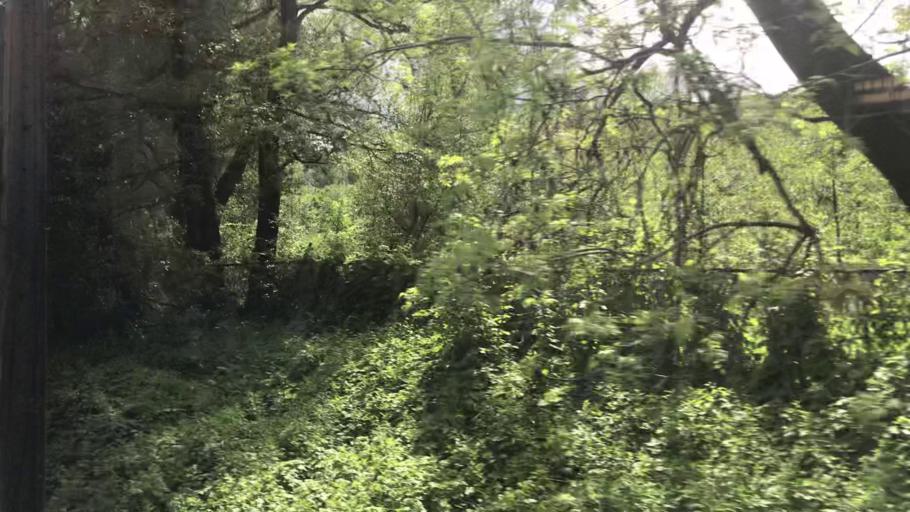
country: PL
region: Lower Silesian Voivodeship
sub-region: Powiat swidnicki
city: Swiebodzice
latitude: 50.8492
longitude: 16.3354
